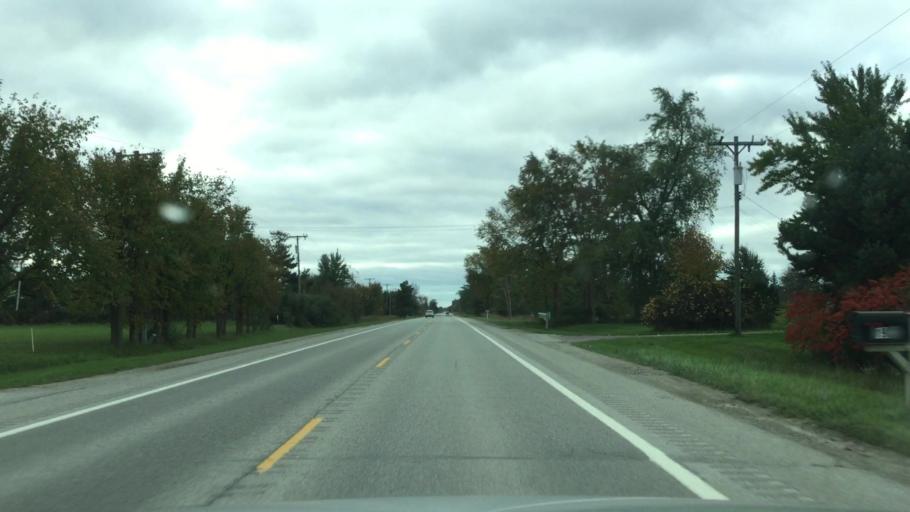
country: US
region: Michigan
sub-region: Macomb County
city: Memphis
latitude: 42.9537
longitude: -82.7631
